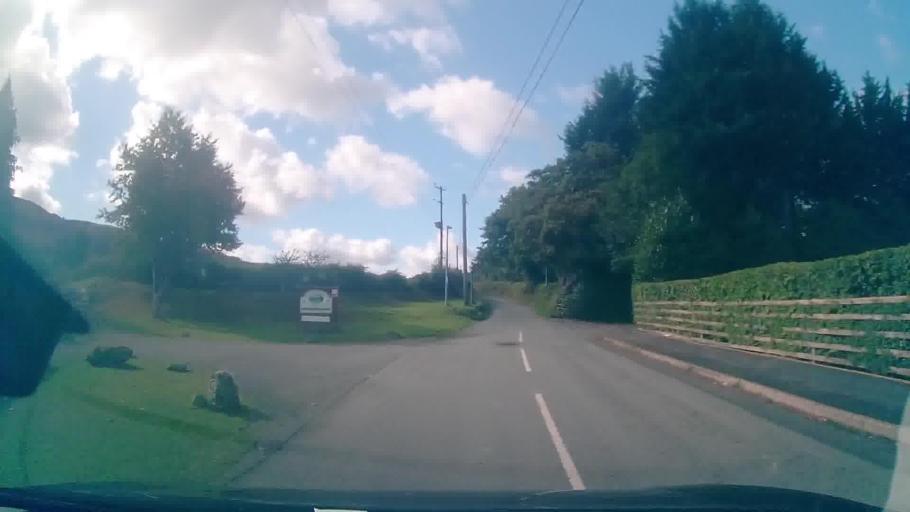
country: GB
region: Wales
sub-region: Sir Powys
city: Llangynog
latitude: 52.8095
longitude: -3.3593
